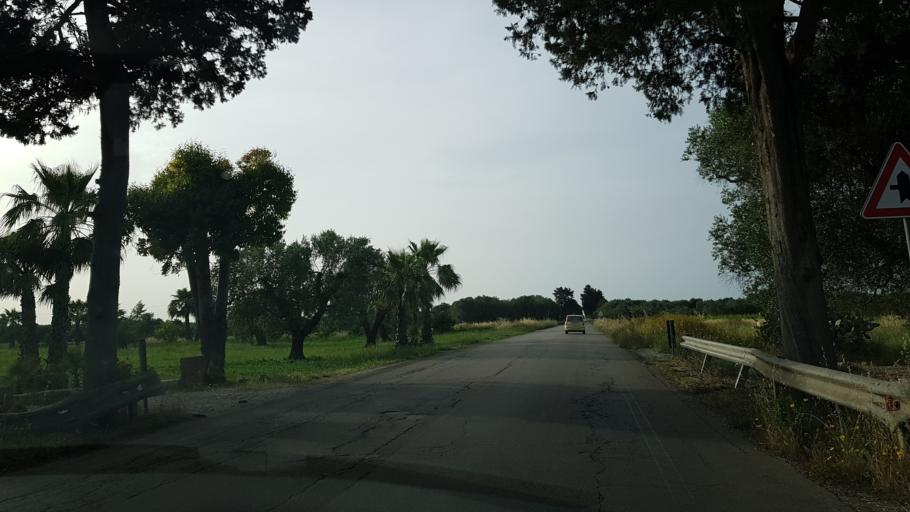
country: IT
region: Apulia
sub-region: Provincia di Brindisi
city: San Pietro Vernotico
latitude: 40.5215
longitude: 17.9860
